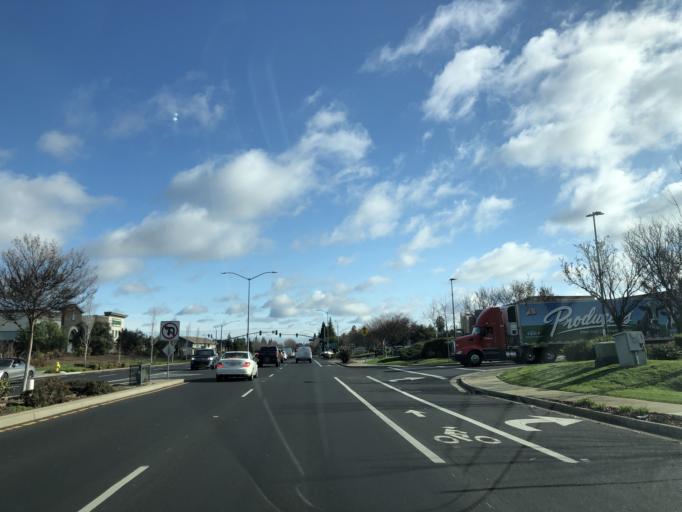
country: US
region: California
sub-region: Contra Costa County
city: Brentwood
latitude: 37.9435
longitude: -121.7364
